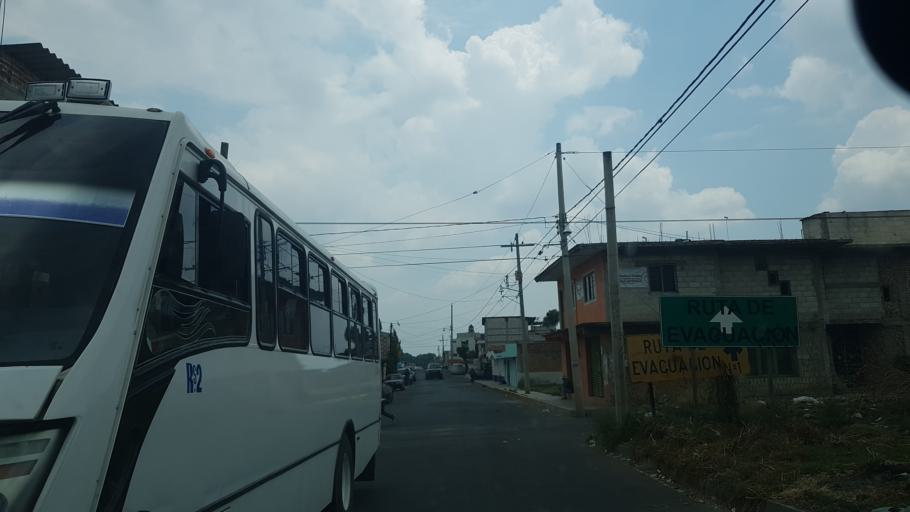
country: MX
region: Puebla
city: Huejotzingo
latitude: 19.1592
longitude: -98.4143
